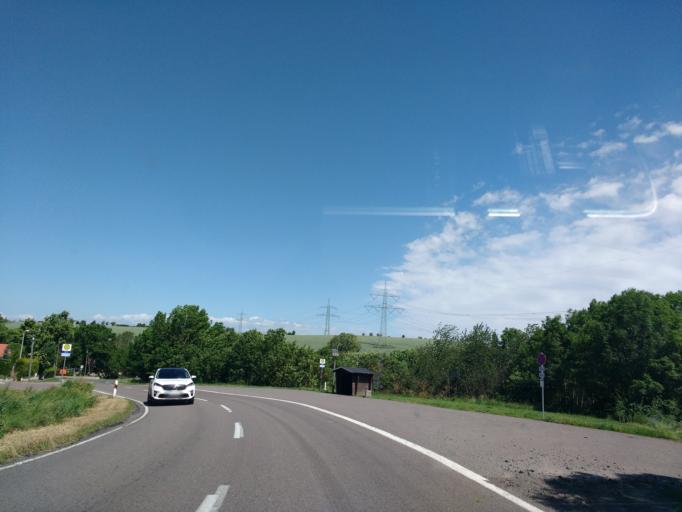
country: DE
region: Saxony-Anhalt
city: Schraplau
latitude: 51.4314
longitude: 11.6514
